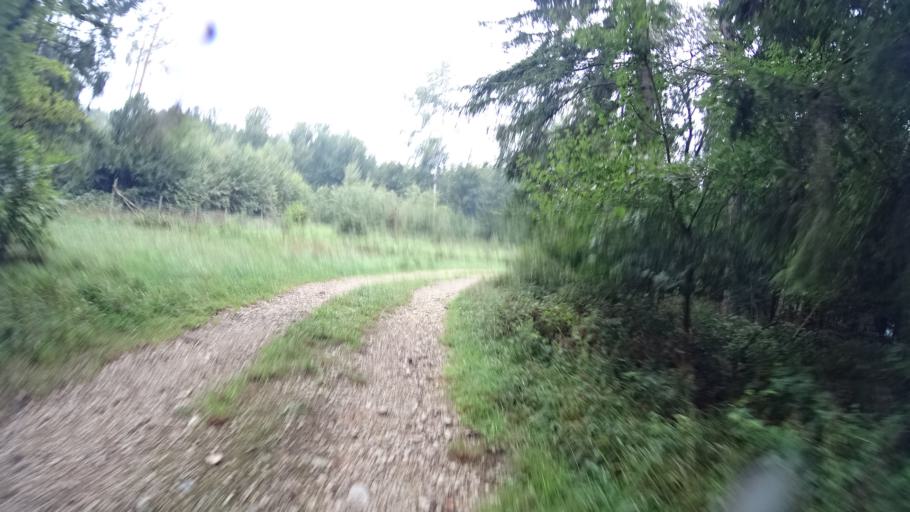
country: DE
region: Bavaria
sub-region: Upper Bavaria
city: Denkendorf
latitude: 48.9197
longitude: 11.4190
